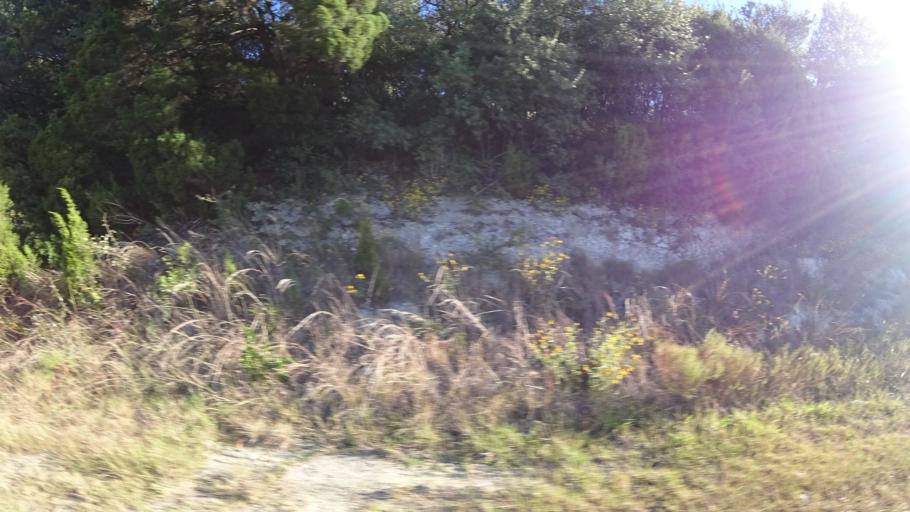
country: US
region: Texas
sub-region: Travis County
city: West Lake Hills
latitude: 30.3627
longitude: -97.8177
